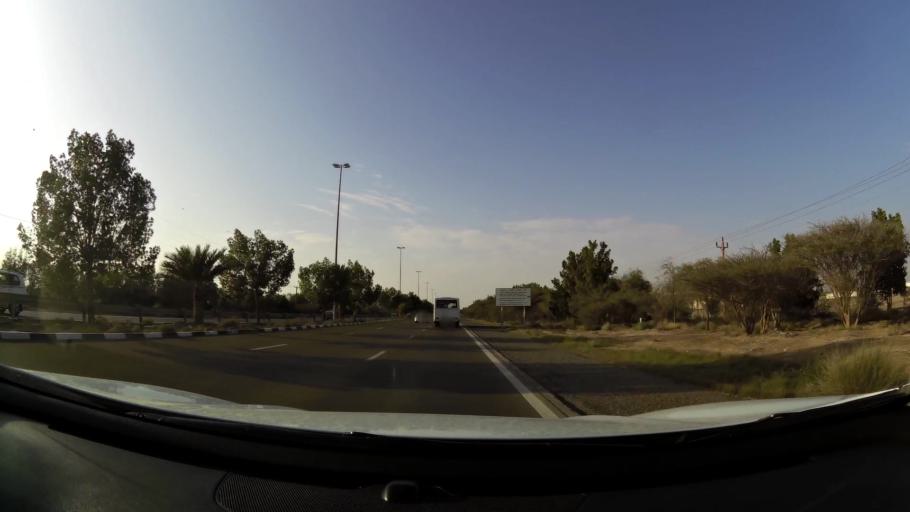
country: AE
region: Abu Dhabi
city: Al Ain
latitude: 24.1370
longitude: 55.8166
